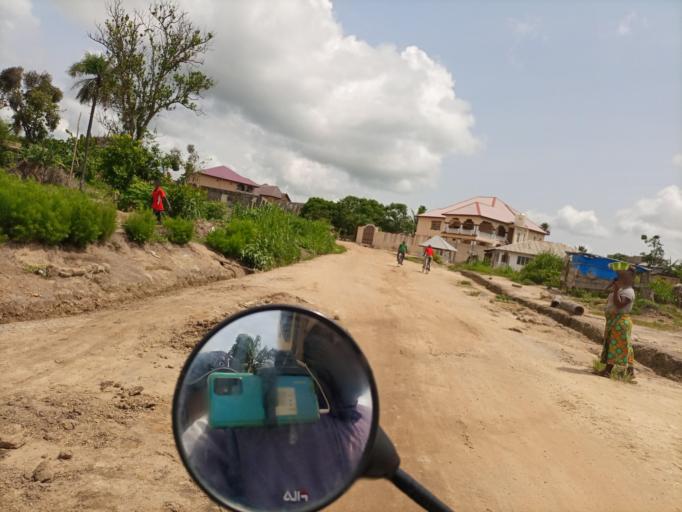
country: SL
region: Southern Province
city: Bo
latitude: 7.9774
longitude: -11.7681
